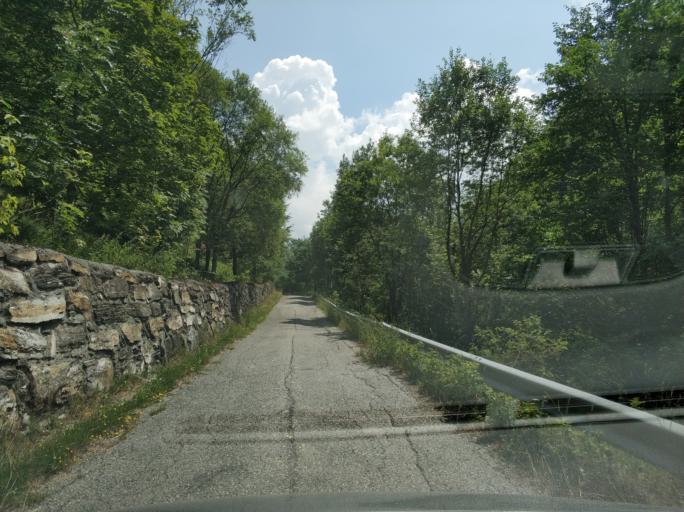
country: IT
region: Piedmont
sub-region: Provincia di Torino
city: Usseglio
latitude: 45.2378
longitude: 7.1993
